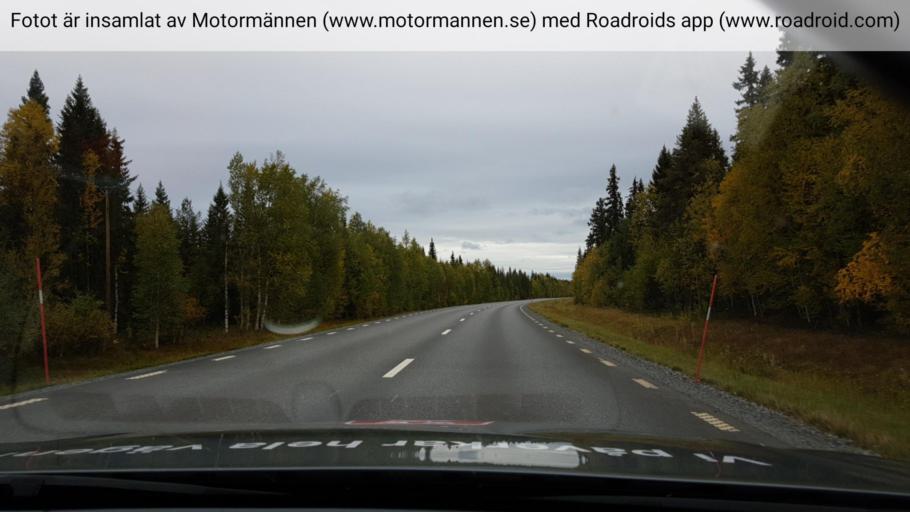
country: SE
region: Vaesterbotten
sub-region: Dorotea Kommun
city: Dorotea
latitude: 64.3118
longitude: 16.6050
